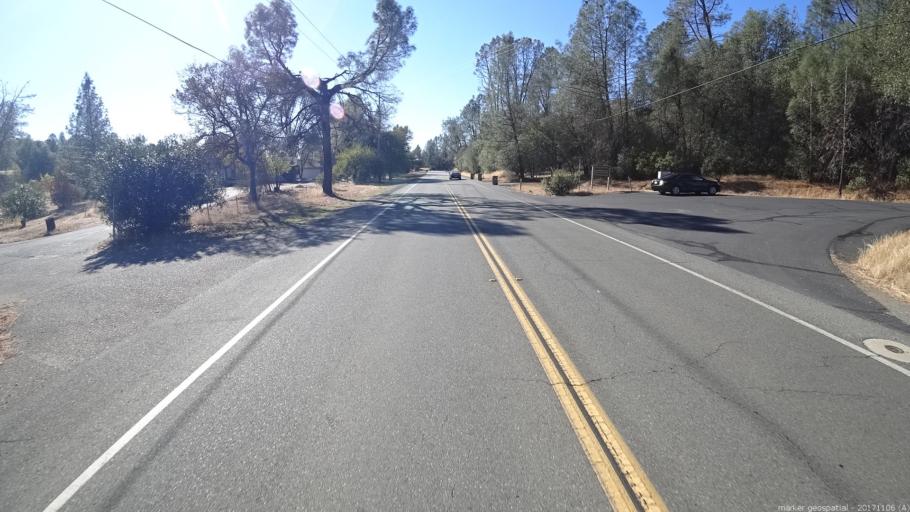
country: US
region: California
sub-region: Shasta County
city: Palo Cedro
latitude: 40.5918
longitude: -122.2958
